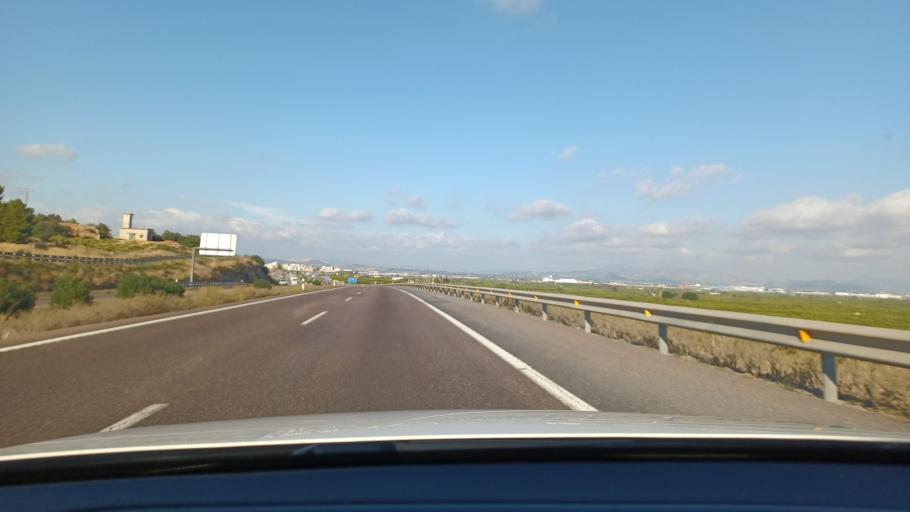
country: ES
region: Valencia
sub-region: Provincia de Castello
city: Betxi
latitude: 39.9067
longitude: -0.1956
